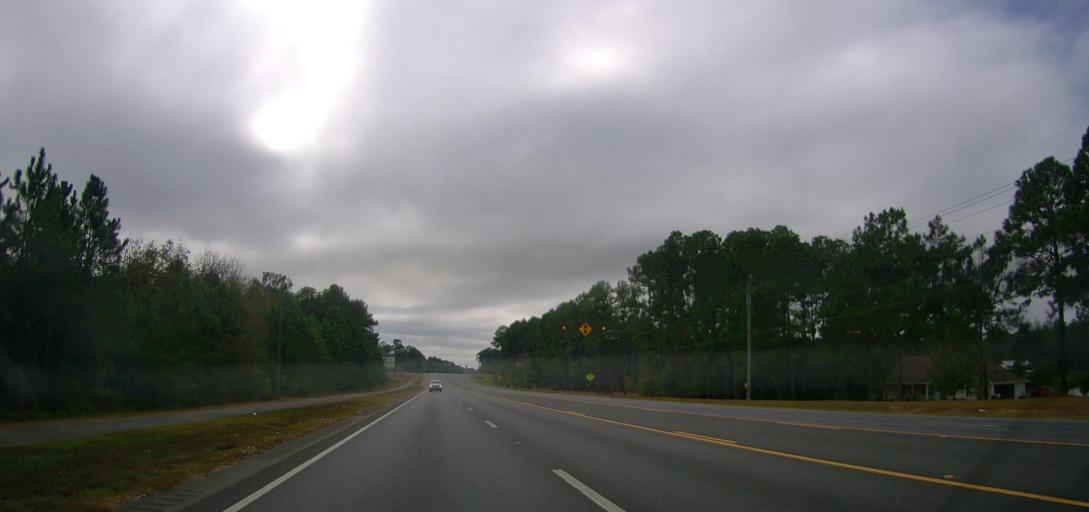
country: US
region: Georgia
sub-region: Colquitt County
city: Moultrie
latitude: 31.1070
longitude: -83.7918
